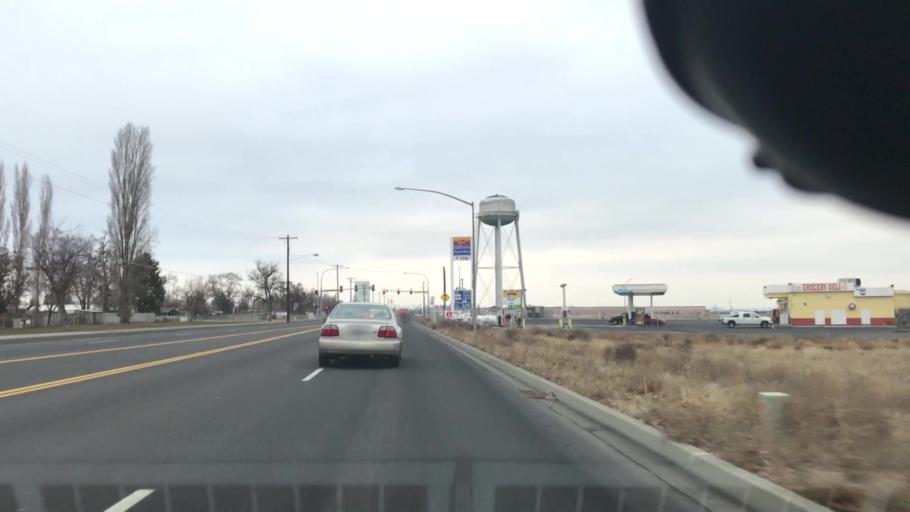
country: US
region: Washington
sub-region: Grant County
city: Cascade Valley
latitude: 47.1623
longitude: -119.3131
